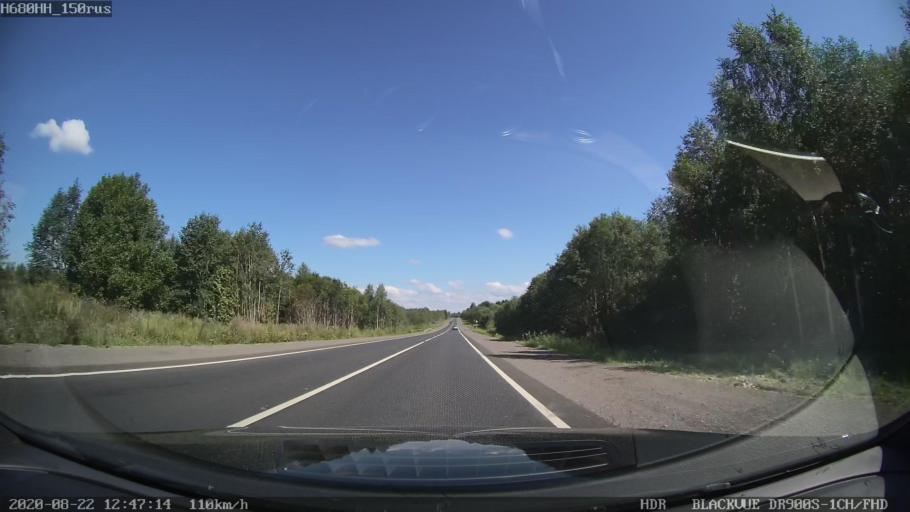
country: RU
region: Tverskaya
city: Rameshki
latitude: 57.4280
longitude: 36.1611
